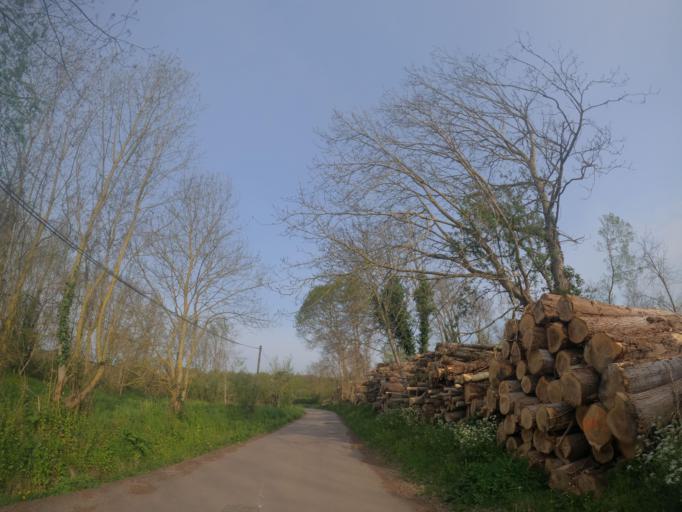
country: FR
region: Poitou-Charentes
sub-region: Departement des Deux-Sevres
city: Saint-Jean-de-Thouars
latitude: 46.9230
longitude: -0.1876
